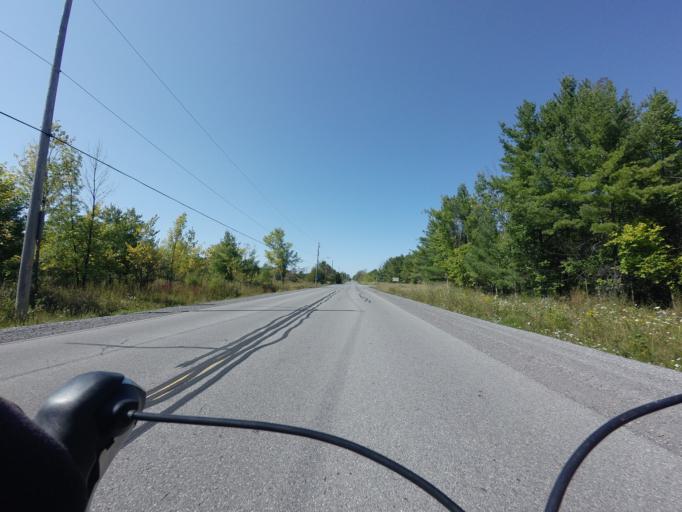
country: CA
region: Ontario
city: Bells Corners
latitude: 45.4324
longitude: -75.9621
